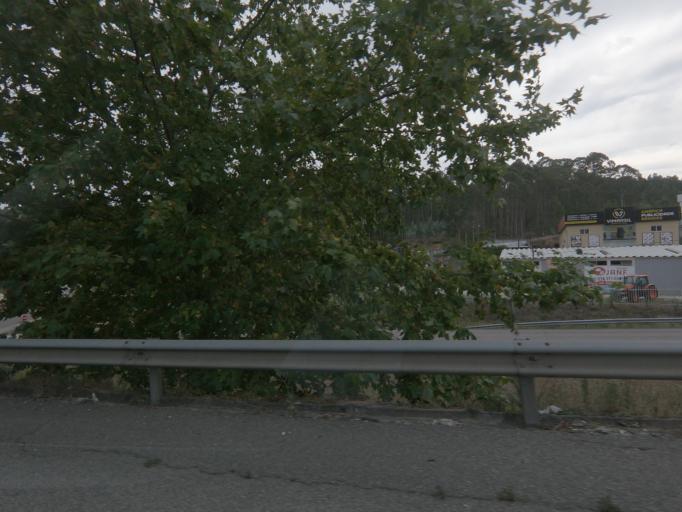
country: PT
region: Coimbra
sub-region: Penacova
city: Lorvao
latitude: 40.3030
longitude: -8.3194
